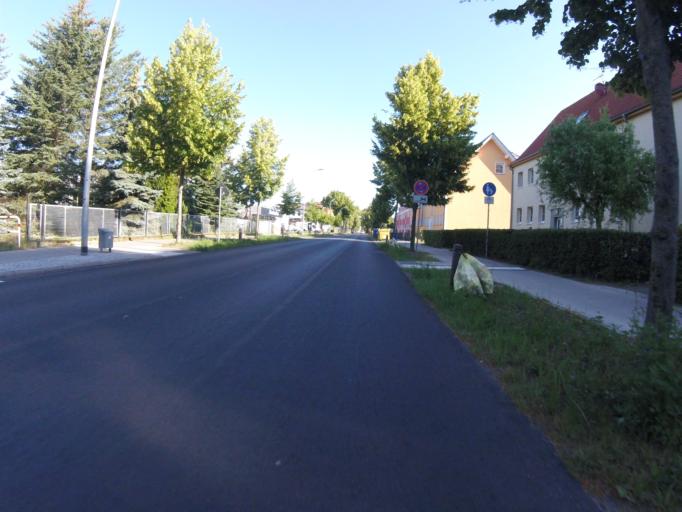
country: DE
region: Brandenburg
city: Konigs Wusterhausen
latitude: 52.2913
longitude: 13.6275
